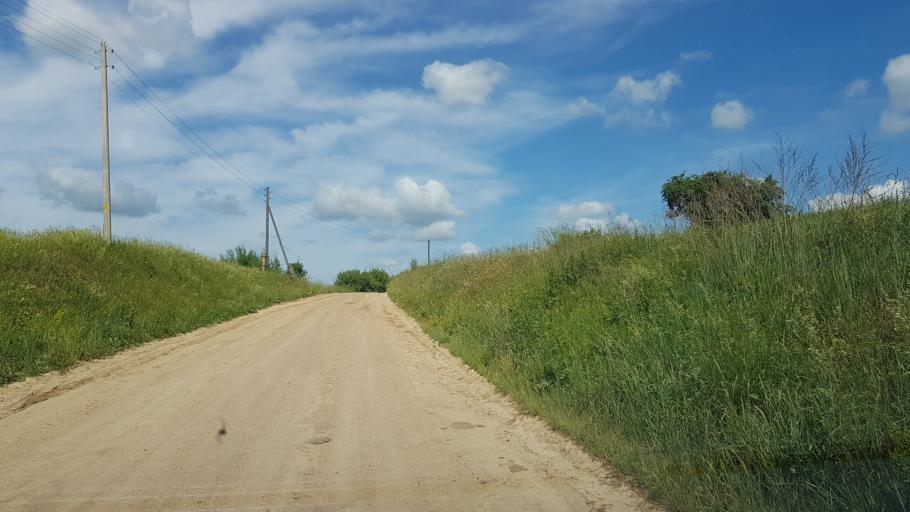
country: BY
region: Vitebsk
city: Dubrowna
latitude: 54.4862
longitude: 30.7974
